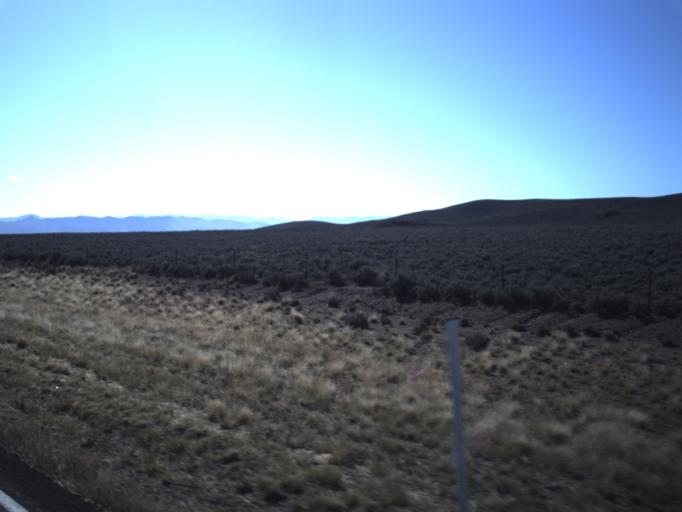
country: US
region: Utah
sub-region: Washington County
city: Enterprise
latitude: 37.7351
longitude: -113.7278
